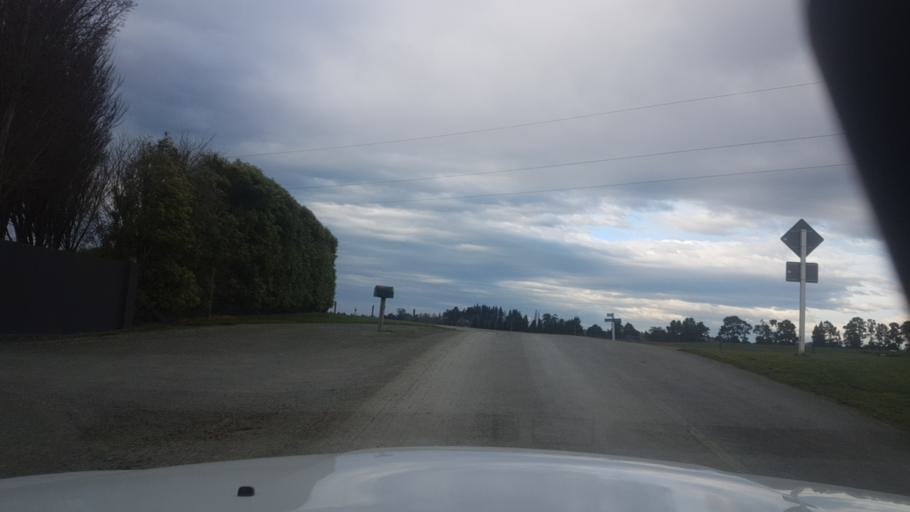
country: NZ
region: Canterbury
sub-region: Timaru District
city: Pleasant Point
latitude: -44.3546
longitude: 171.1559
